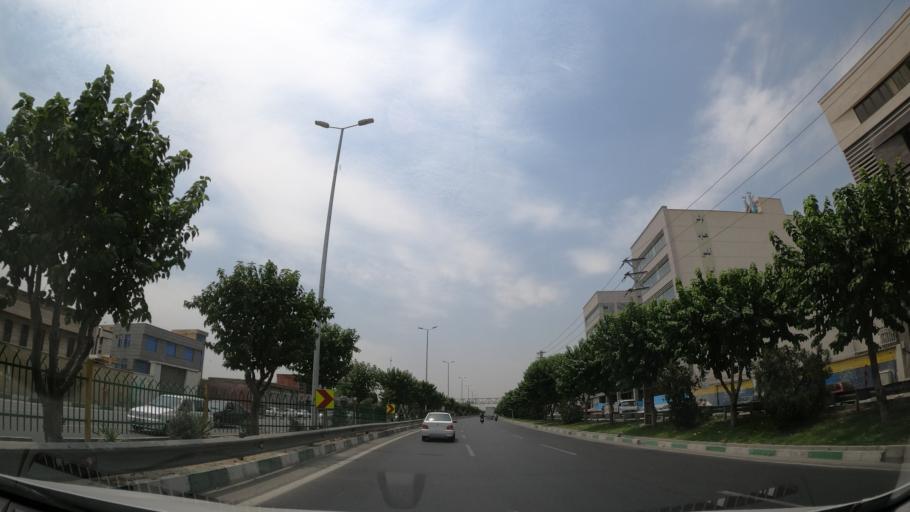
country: IR
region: Tehran
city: Tehran
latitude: 35.6750
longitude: 51.3243
